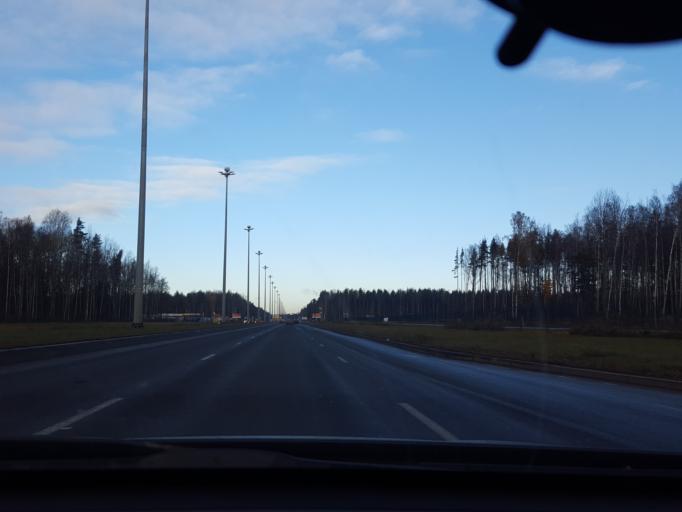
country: RU
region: Leningrad
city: Untolovo
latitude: 60.0488
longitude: 30.2319
